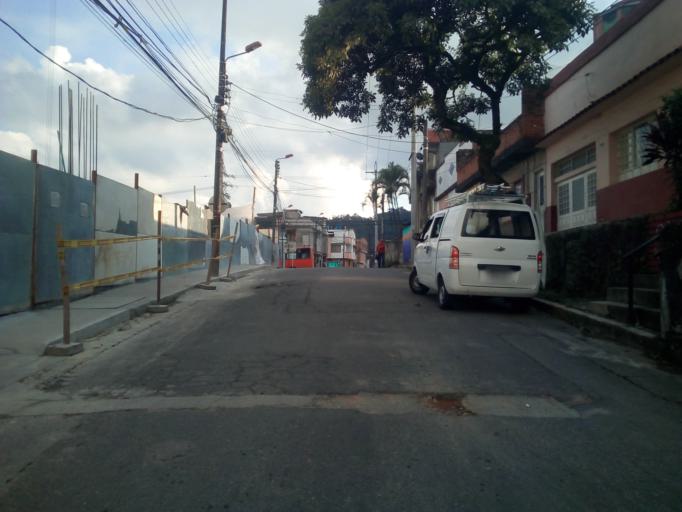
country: CO
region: Tolima
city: Ibague
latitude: 4.4495
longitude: -75.2465
